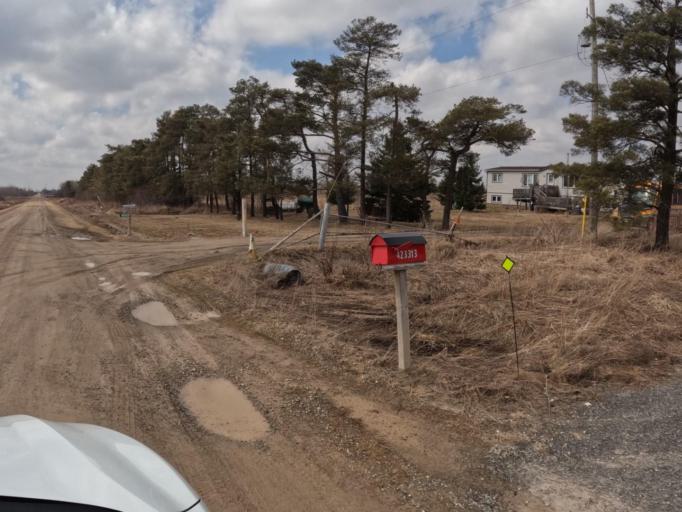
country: CA
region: Ontario
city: Shelburne
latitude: 44.0218
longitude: -80.2913
